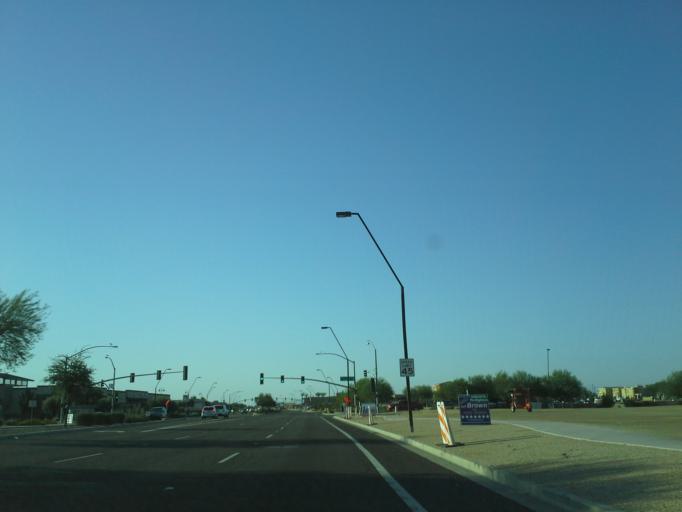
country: US
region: Arizona
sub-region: Maricopa County
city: Queen Creek
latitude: 33.2505
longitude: -111.6377
